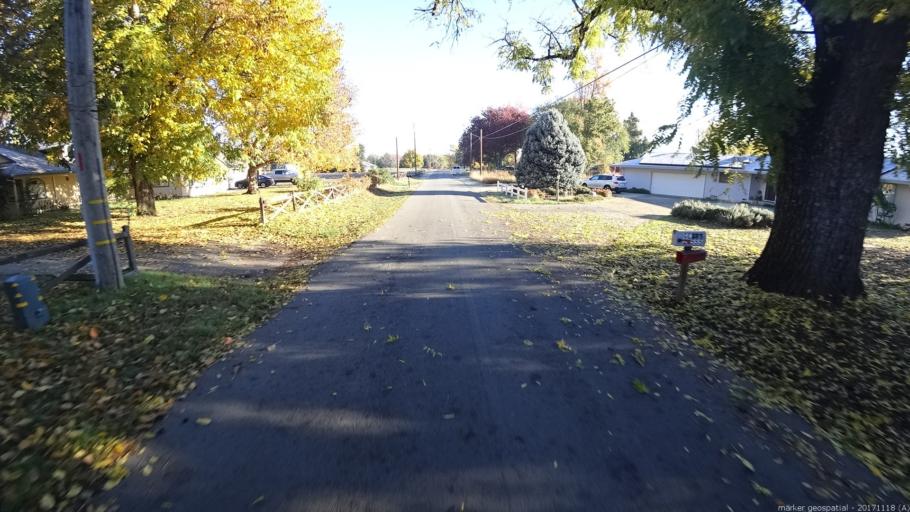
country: US
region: California
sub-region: Shasta County
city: Anderson
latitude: 40.4565
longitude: -122.2542
